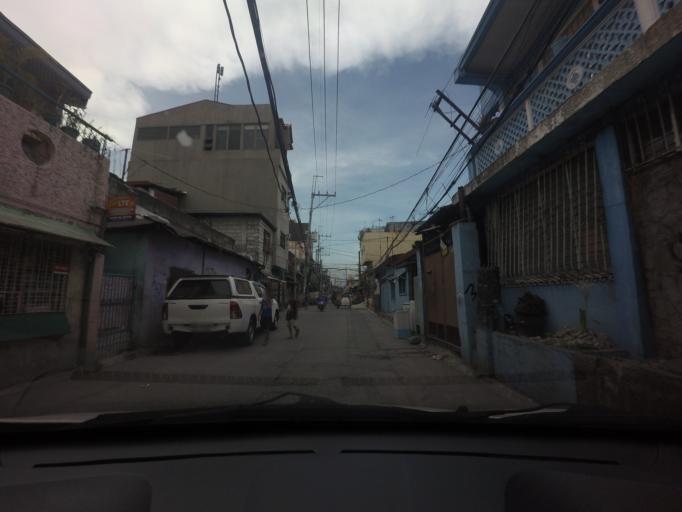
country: PH
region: Calabarzon
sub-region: Province of Rizal
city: Pateros
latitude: 14.5379
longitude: 121.0604
